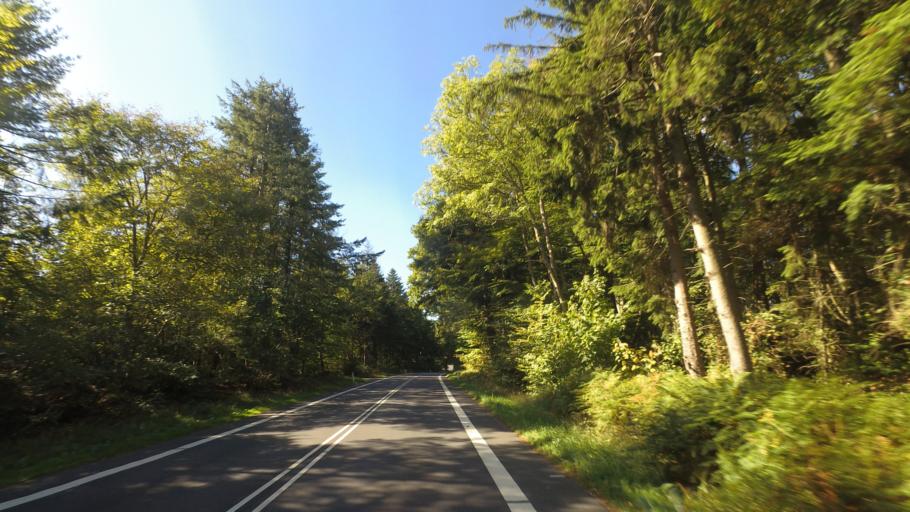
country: DK
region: Capital Region
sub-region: Bornholm Kommune
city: Akirkeby
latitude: 55.0649
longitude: 15.0168
